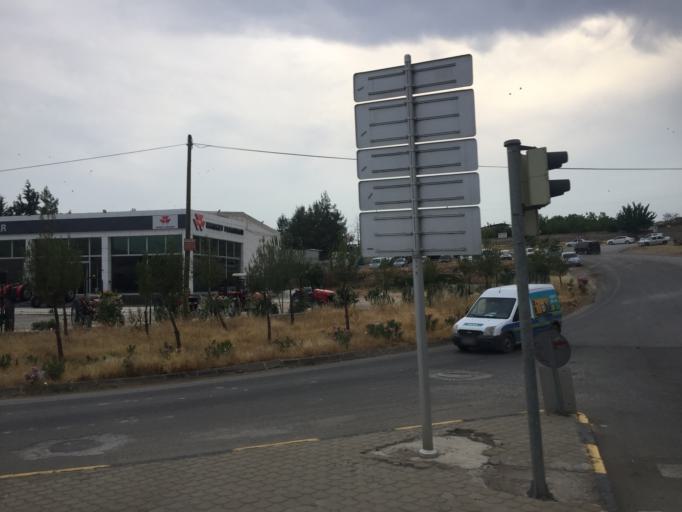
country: TR
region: Gaziantep
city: Gaziantep
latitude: 37.0217
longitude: 37.4285
